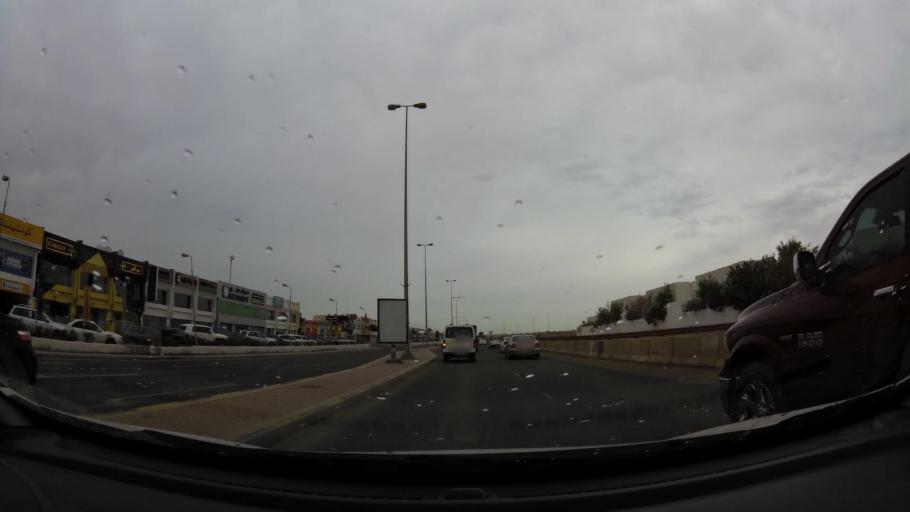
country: BH
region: Central Governorate
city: Madinat Hamad
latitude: 26.1654
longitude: 50.4697
